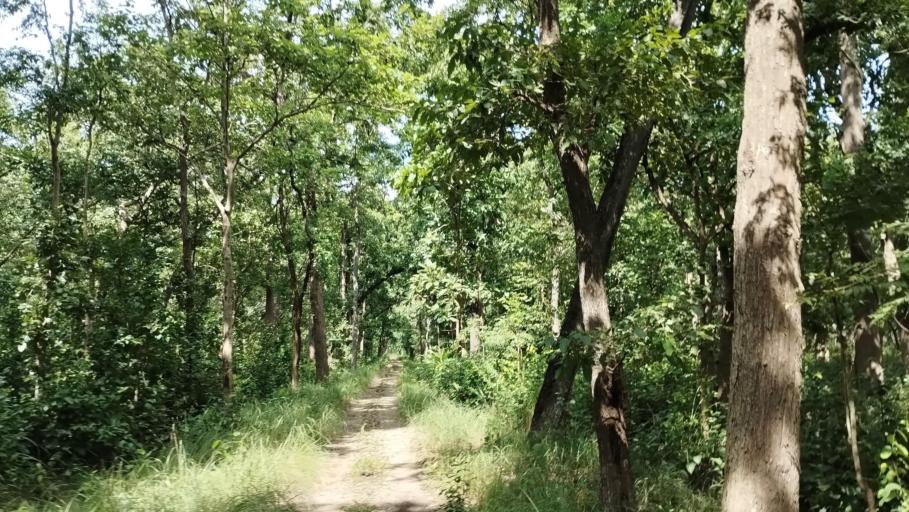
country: NP
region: Far Western
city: Tikapur
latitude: 28.5154
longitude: 81.2729
